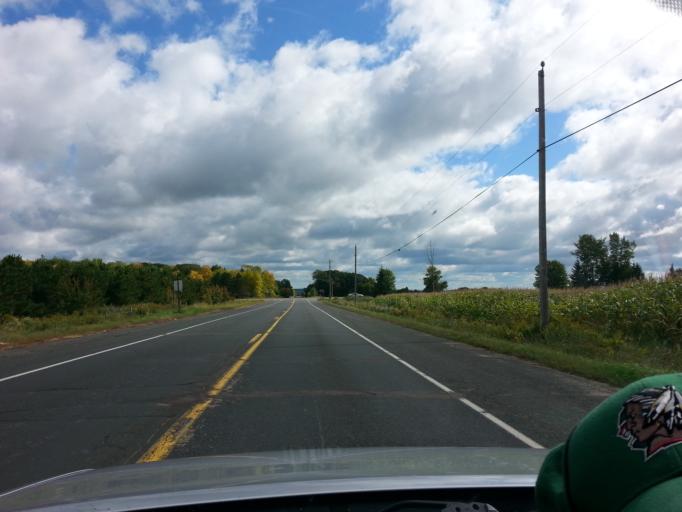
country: US
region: Minnesota
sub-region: Washington County
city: Oakdale
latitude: 44.9706
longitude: -92.9362
